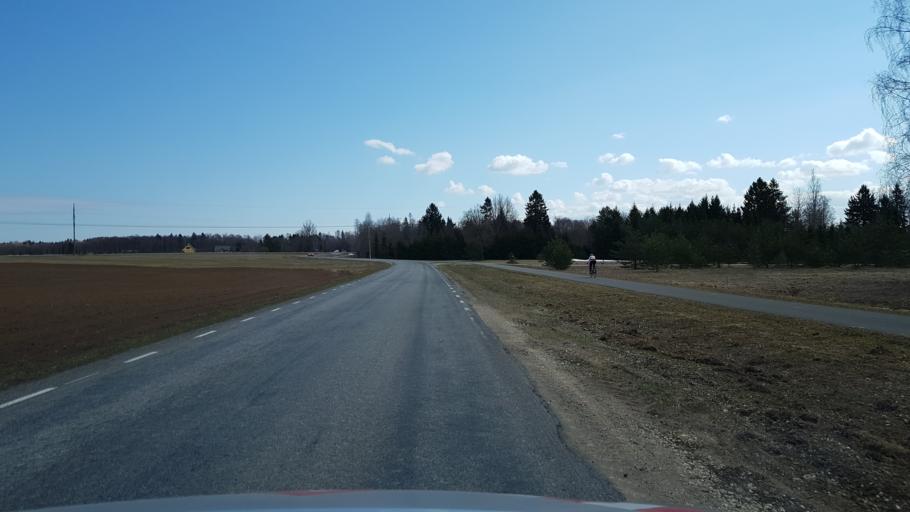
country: EE
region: Laeaene-Virumaa
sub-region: Rakvere linn
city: Rakvere
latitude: 59.3830
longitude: 26.3105
